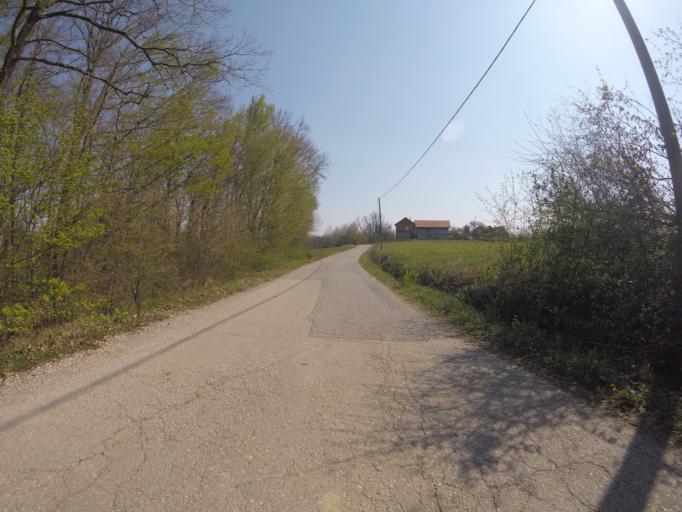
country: HR
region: Grad Zagreb
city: Strmec
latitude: 45.5902
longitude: 15.9234
